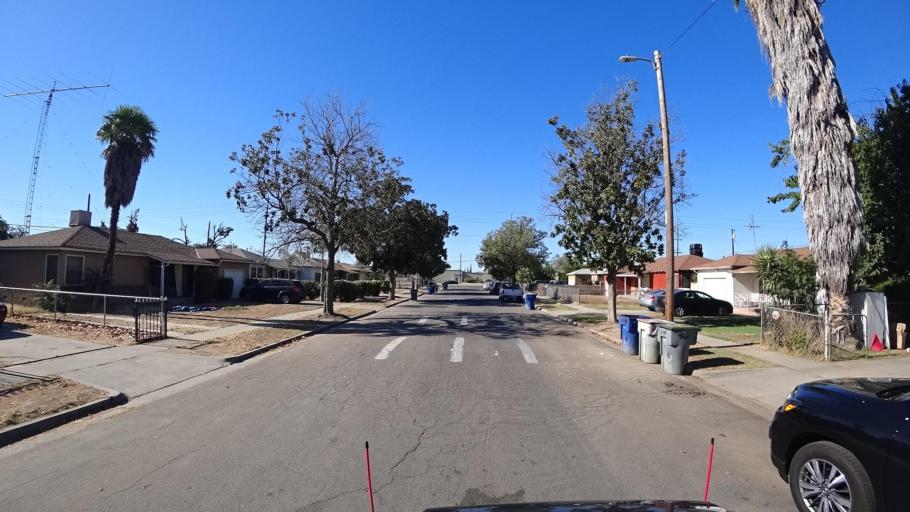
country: US
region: California
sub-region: Fresno County
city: Fresno
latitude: 36.7077
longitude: -119.7885
